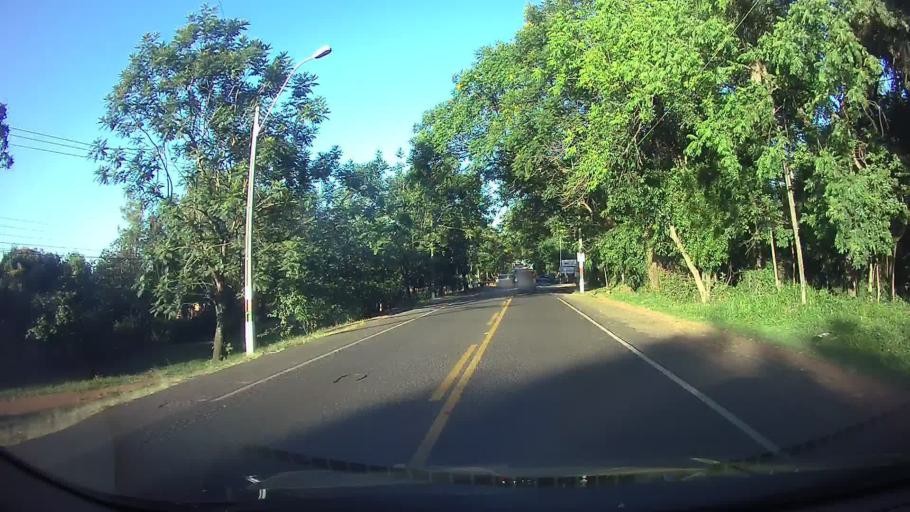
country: PY
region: Central
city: Aregua
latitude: -25.3231
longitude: -57.3921
